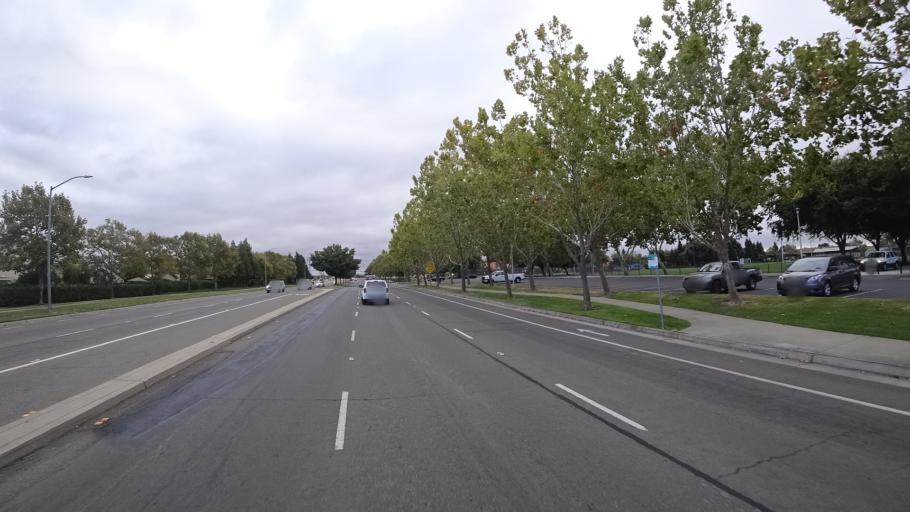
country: US
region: California
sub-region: Sacramento County
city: Laguna
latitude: 38.4305
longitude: -121.4212
